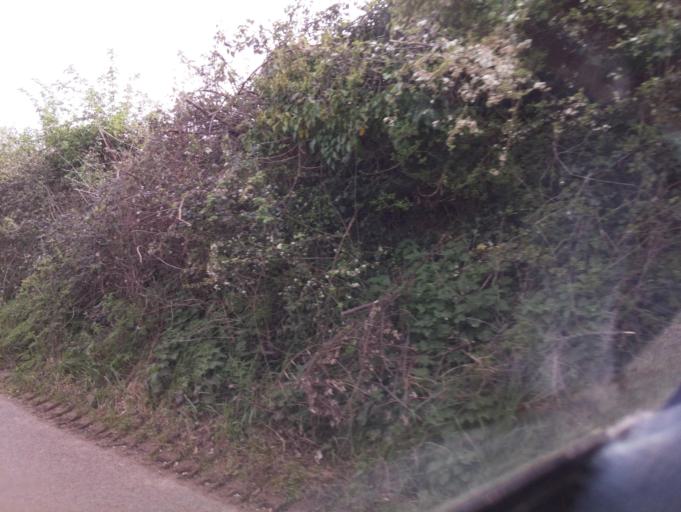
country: GB
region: England
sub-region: Dorset
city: Sherborne
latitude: 50.9568
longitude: -2.5091
